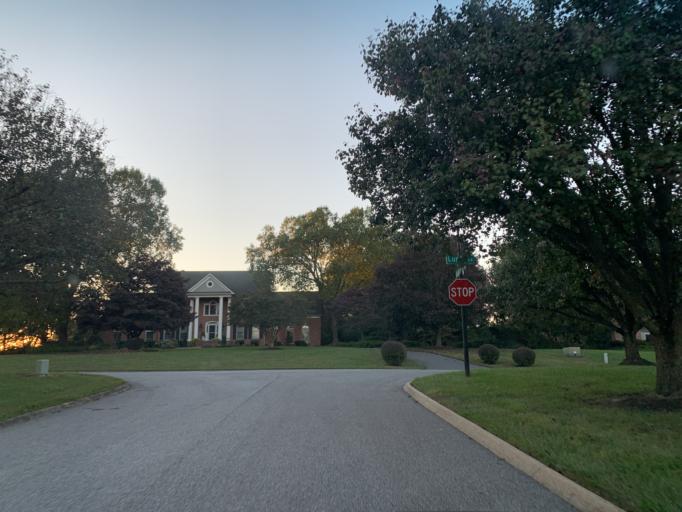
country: US
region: Maryland
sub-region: Harford County
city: Bel Air South
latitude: 39.5181
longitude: -76.2905
